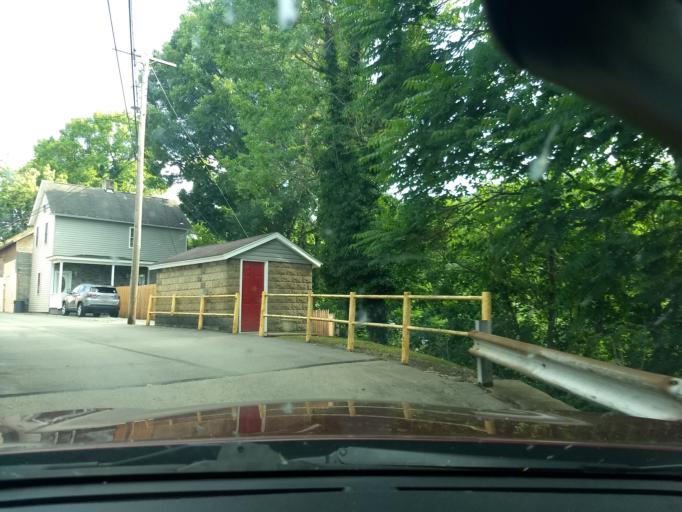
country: US
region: Pennsylvania
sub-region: Westmoreland County
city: Irwin
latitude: 40.3309
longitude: -79.7120
